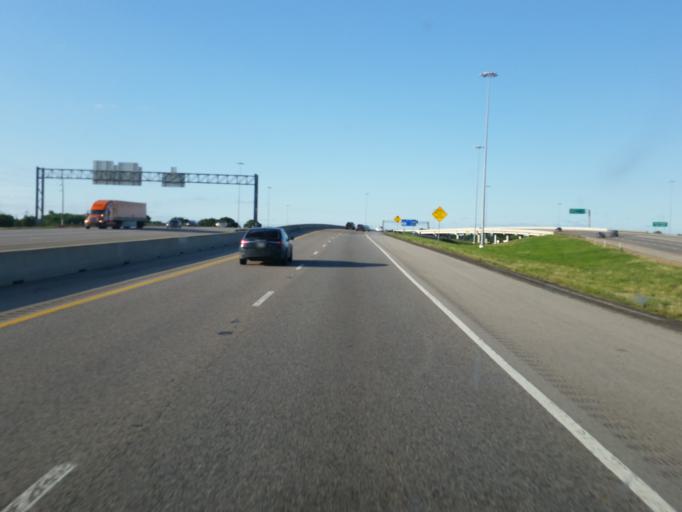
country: US
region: Texas
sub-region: Dallas County
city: Balch Springs
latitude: 32.6975
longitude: -96.6283
